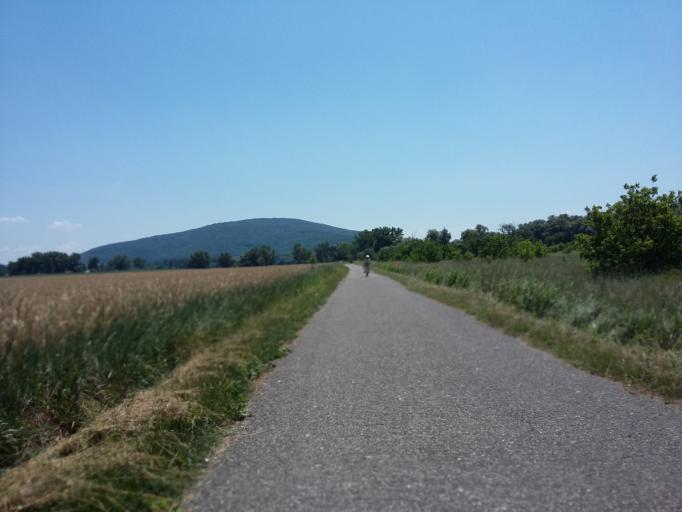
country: AT
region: Lower Austria
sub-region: Politischer Bezirk Ganserndorf
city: Marchegg
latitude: 48.2286
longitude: 16.9577
